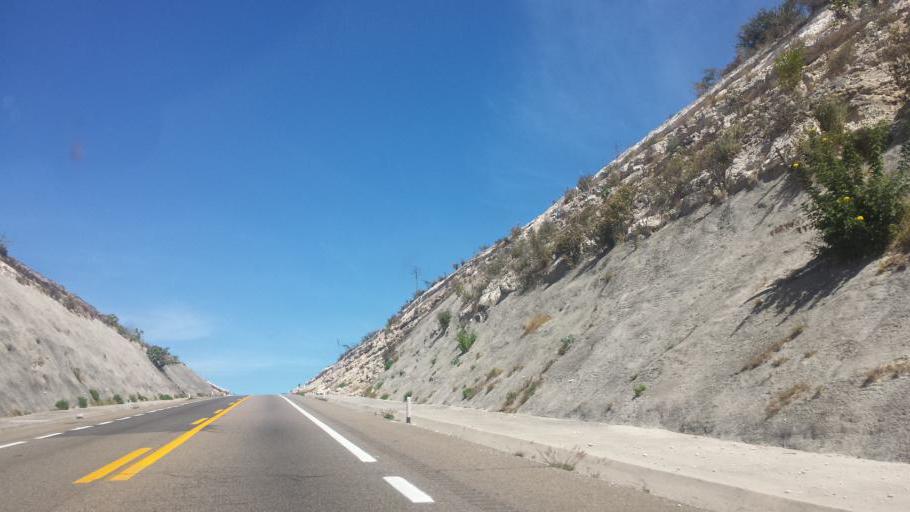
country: MX
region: Oaxaca
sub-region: Villa Tejupam de la Union
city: Villa Tejupam de la Union
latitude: 17.9130
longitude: -97.3629
